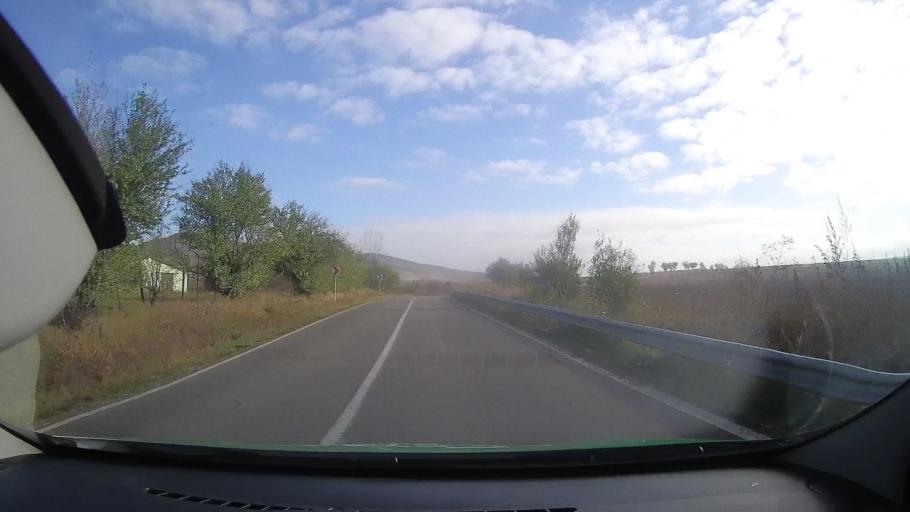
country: RO
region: Tulcea
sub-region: Comuna Bestepe
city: Bestepe
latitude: 45.0818
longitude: 29.0285
